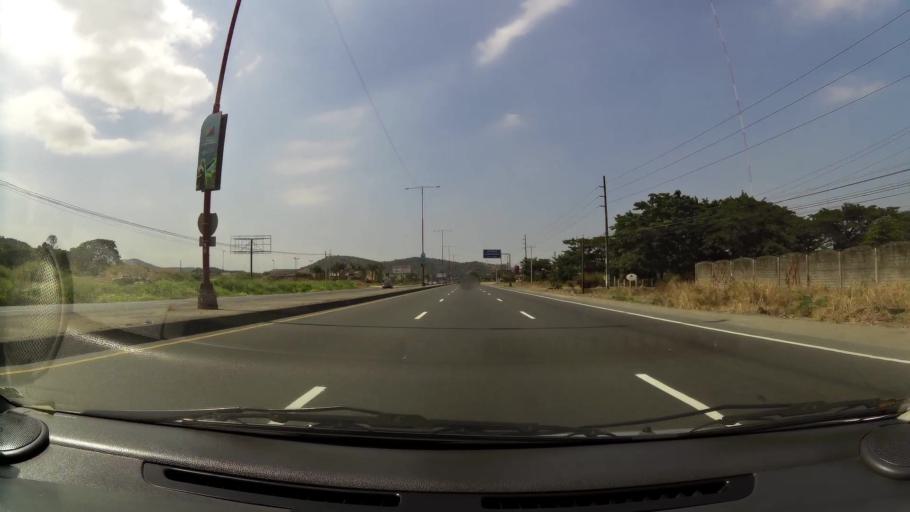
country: EC
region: Guayas
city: El Triunfo
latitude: -2.0553
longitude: -79.9184
